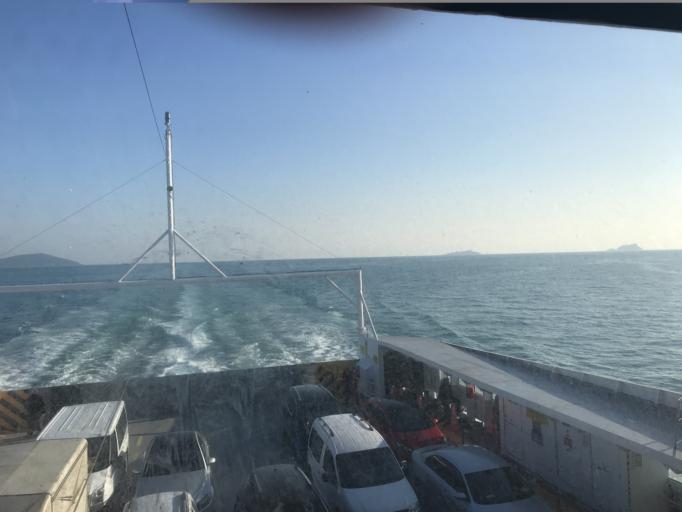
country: TR
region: Istanbul
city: Kinali
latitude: 40.9399
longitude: 28.9990
